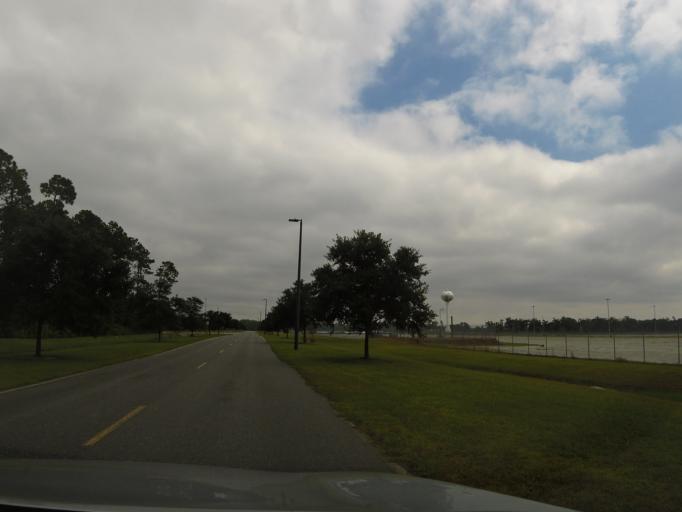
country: US
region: Georgia
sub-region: Glynn County
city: Brunswick
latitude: 31.1120
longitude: -81.5430
